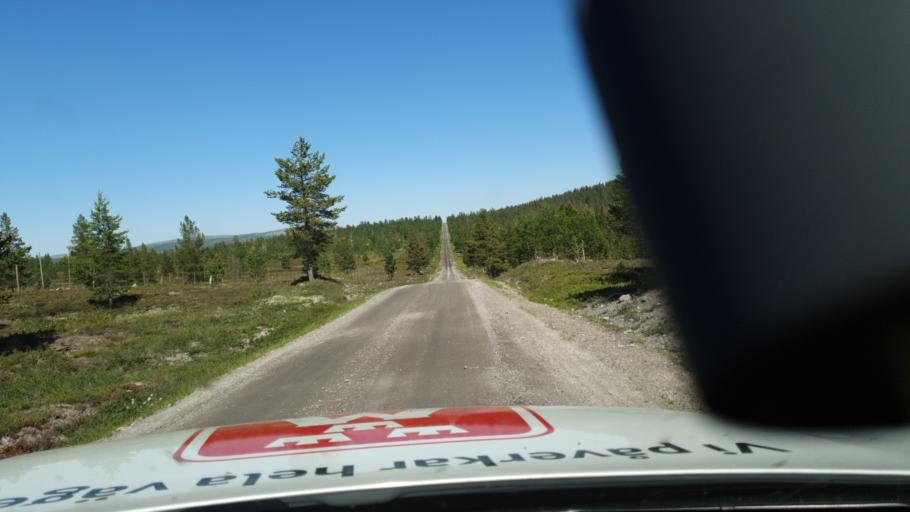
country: NO
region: Hedmark
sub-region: Engerdal
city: Engerdal
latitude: 62.1326
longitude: 12.9191
